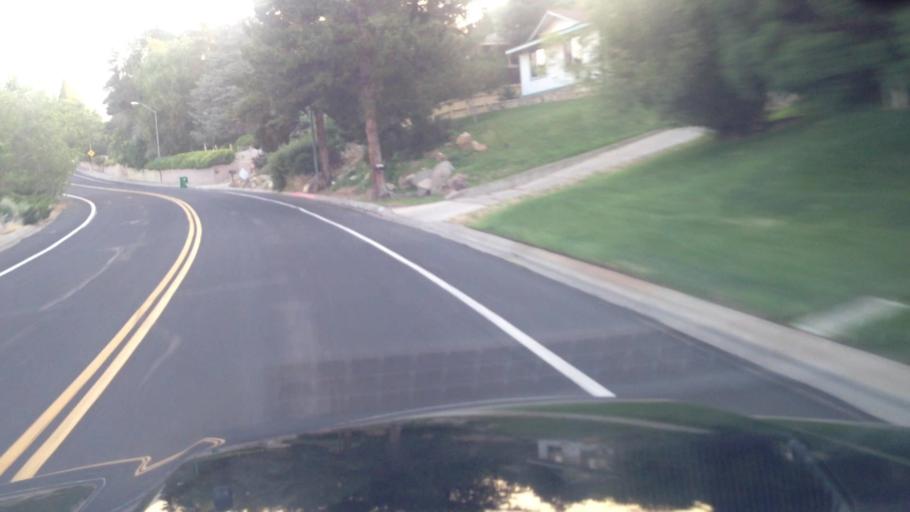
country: US
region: Nevada
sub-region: Washoe County
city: Reno
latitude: 39.4903
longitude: -119.8294
